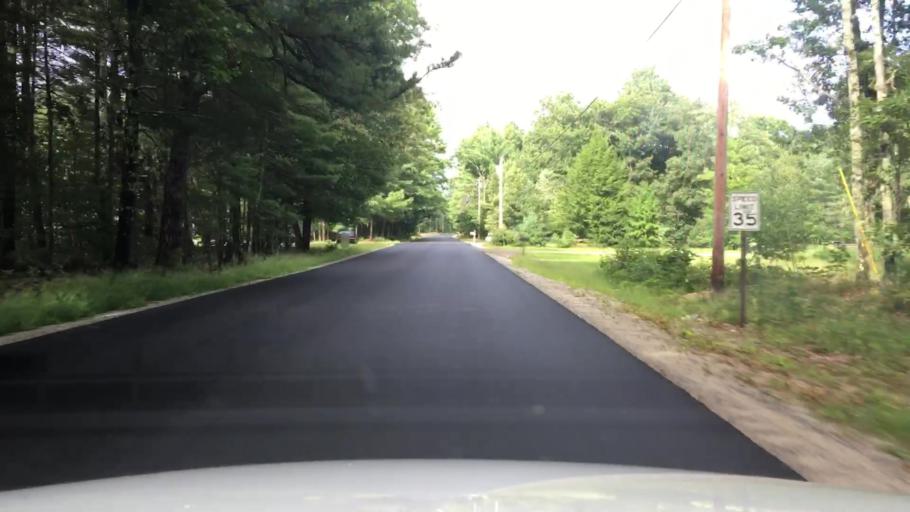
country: US
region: Maine
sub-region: York County
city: West Kennebunk
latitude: 43.4284
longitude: -70.6480
